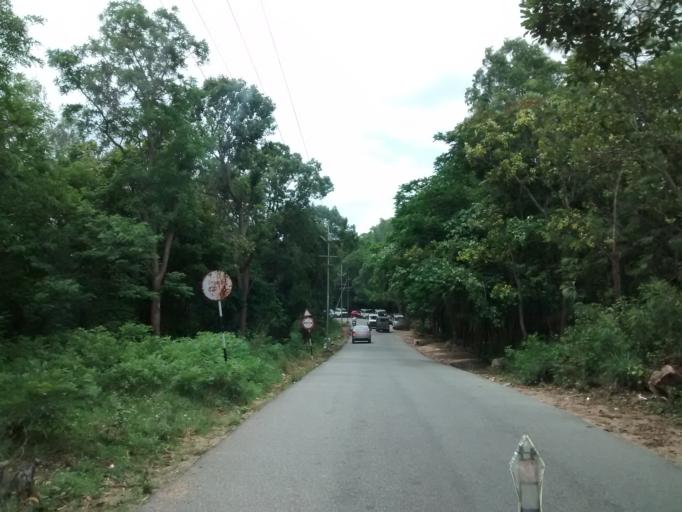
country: IN
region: Andhra Pradesh
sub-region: Chittoor
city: Tirumala
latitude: 13.7043
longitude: 79.3410
